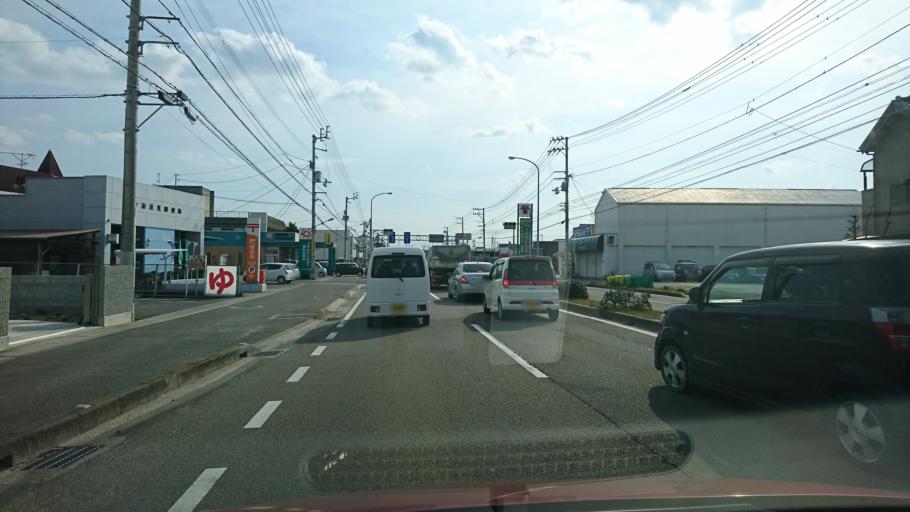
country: JP
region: Ehime
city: Hojo
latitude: 34.0849
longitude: 132.9897
